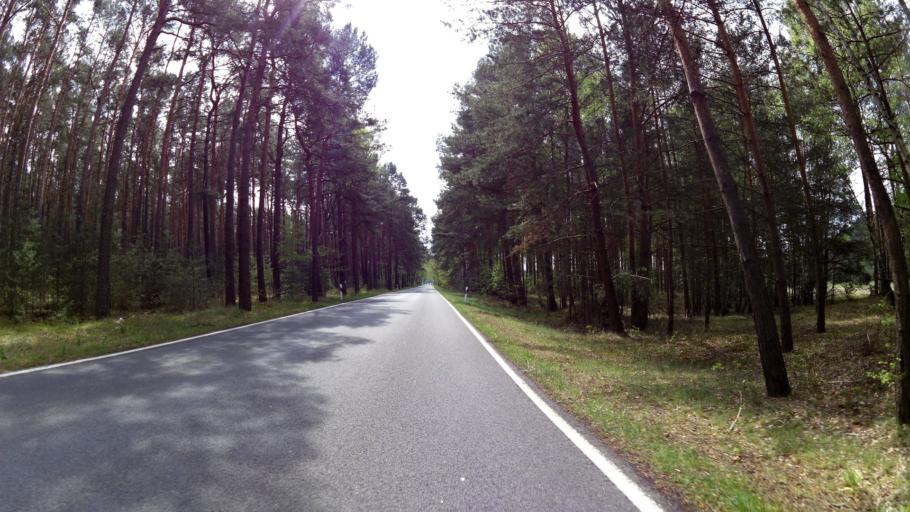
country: DE
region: Brandenburg
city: Bestensee
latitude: 52.2741
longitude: 13.7337
